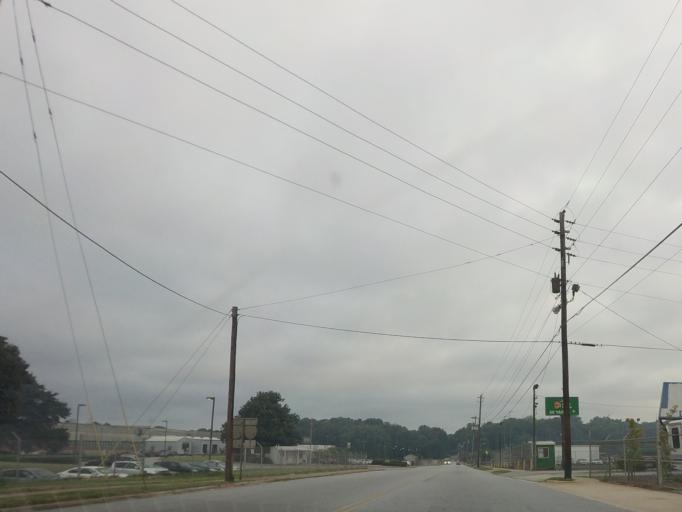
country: US
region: Georgia
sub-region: Fulton County
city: Hapeville
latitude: 33.6674
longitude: -84.4189
